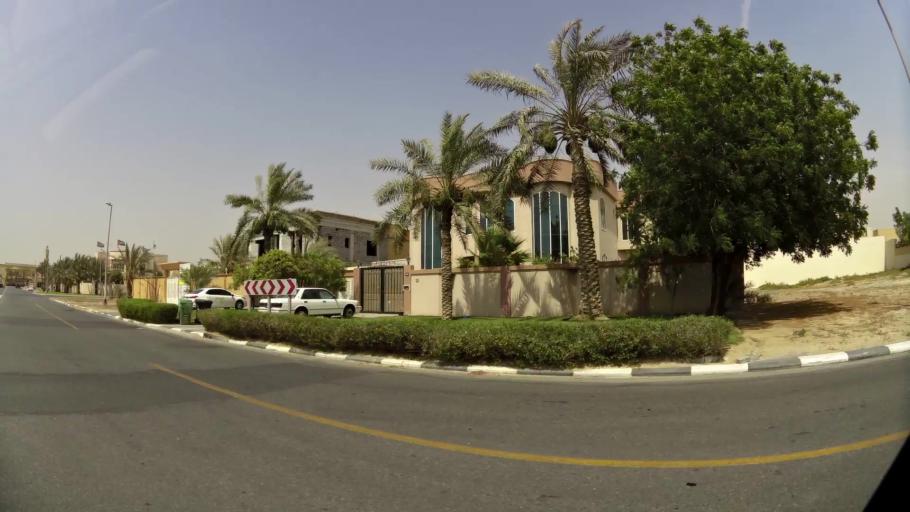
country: AE
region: Ash Shariqah
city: Sharjah
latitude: 25.2399
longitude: 55.4370
